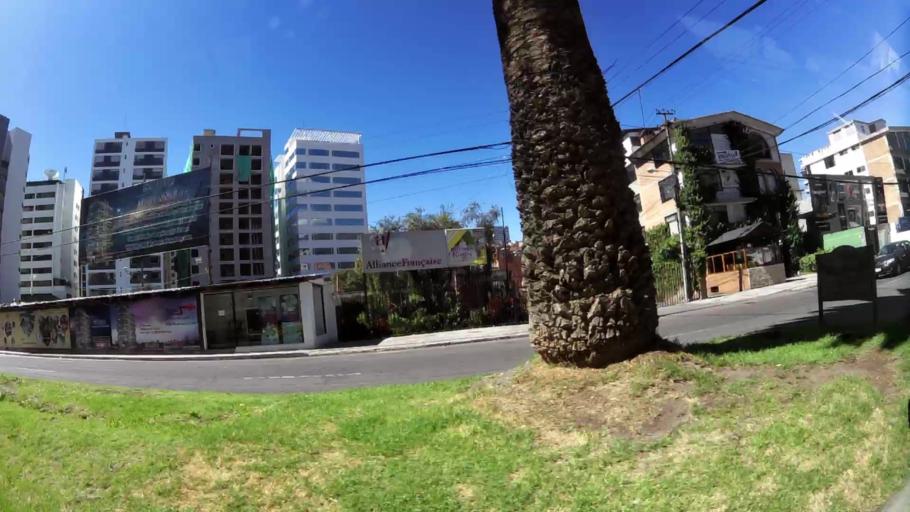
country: EC
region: Pichincha
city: Quito
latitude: -0.1881
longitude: -78.4814
